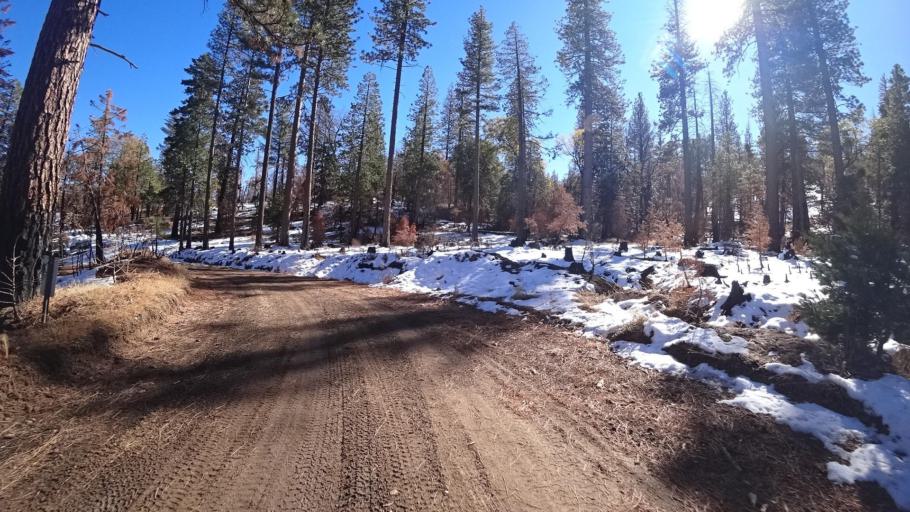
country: US
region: California
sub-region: Kern County
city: Alta Sierra
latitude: 35.7154
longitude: -118.5352
